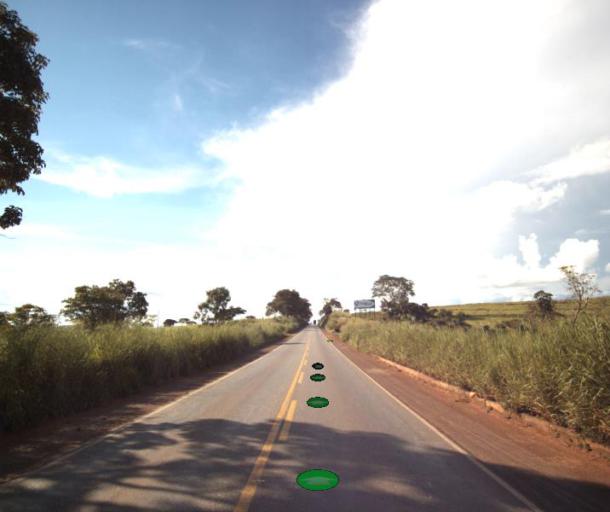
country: BR
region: Goias
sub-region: Rialma
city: Rialma
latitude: -15.3444
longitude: -49.5689
